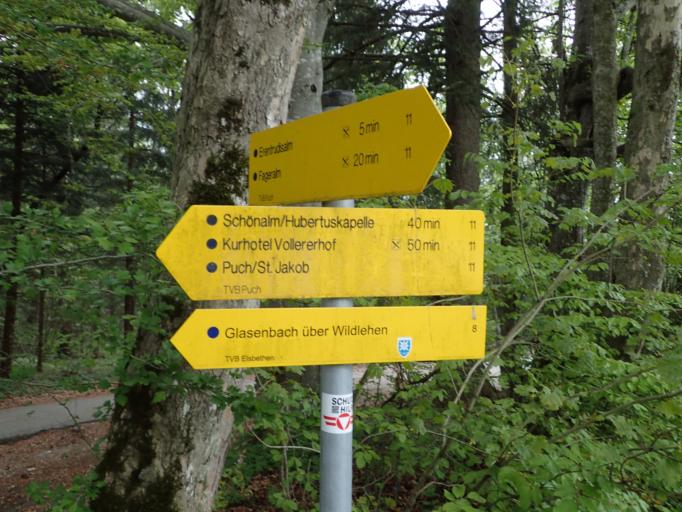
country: AT
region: Salzburg
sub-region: Politischer Bezirk Salzburg-Umgebung
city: Elsbethen
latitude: 47.7527
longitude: 13.1149
